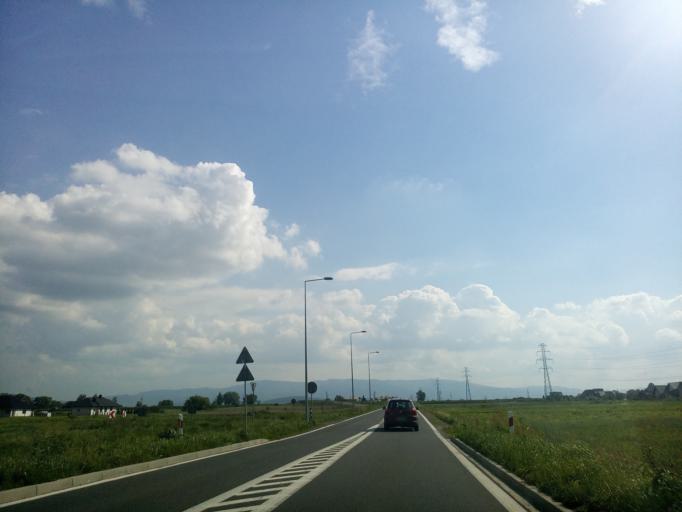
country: PL
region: Lesser Poland Voivodeship
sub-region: Powiat nowosadecki
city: Chelmiec
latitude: 49.6212
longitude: 20.6426
